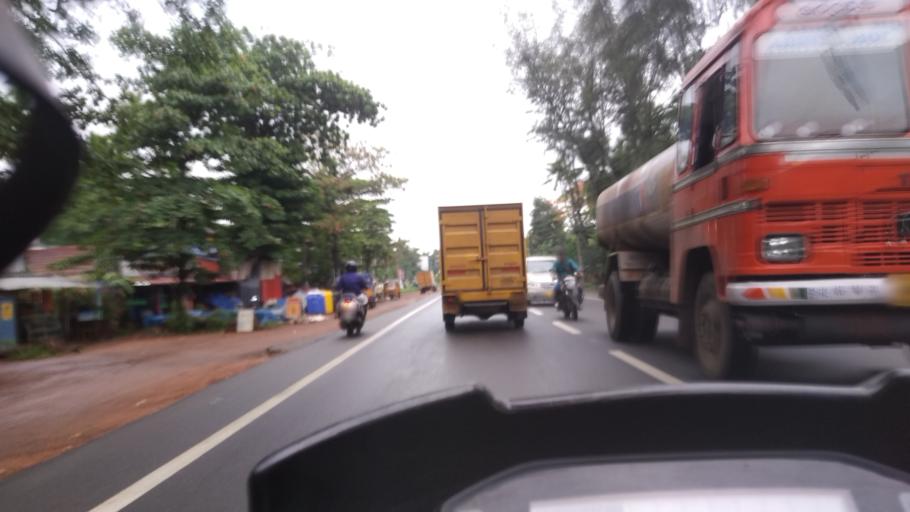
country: IN
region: Kerala
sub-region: Alappuzha
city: Mavelikara
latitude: 9.3158
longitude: 76.4278
